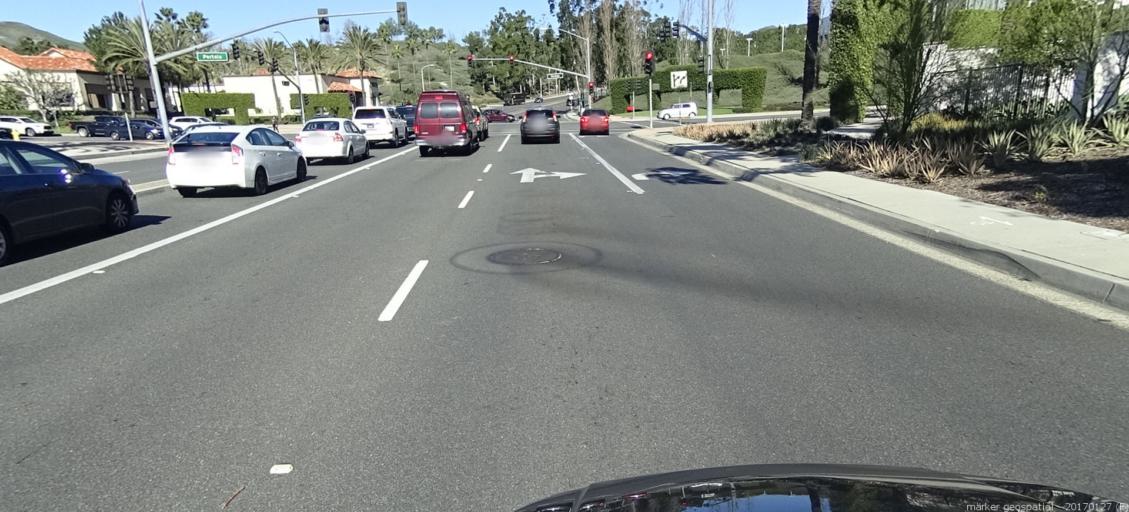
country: US
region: California
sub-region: Orange County
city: Foothill Ranch
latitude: 33.6774
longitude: -117.6622
